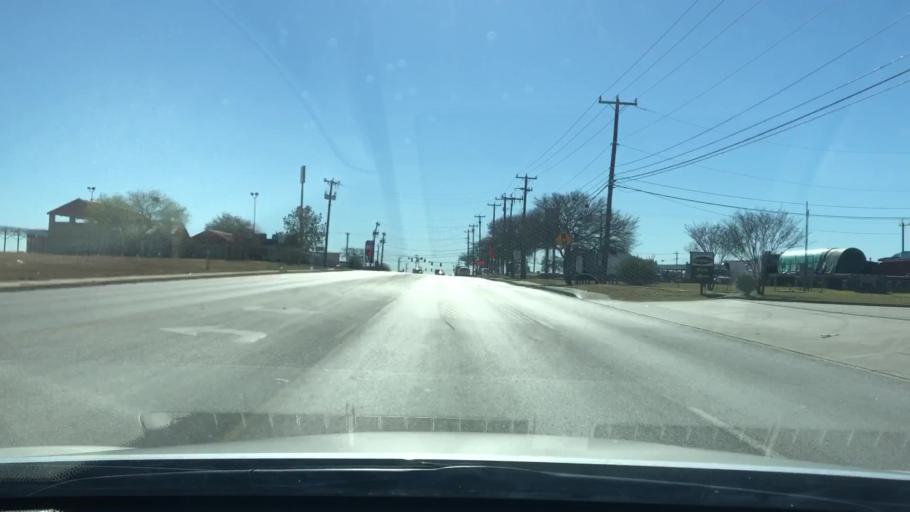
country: US
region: Texas
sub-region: Bexar County
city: Kirby
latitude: 29.4484
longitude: -98.3608
